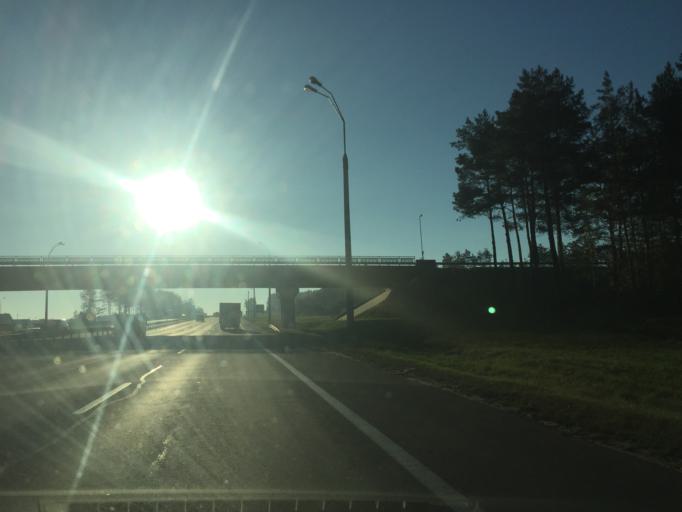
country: BY
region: Minsk
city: Pryvol'ny
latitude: 53.8229
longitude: 27.7574
